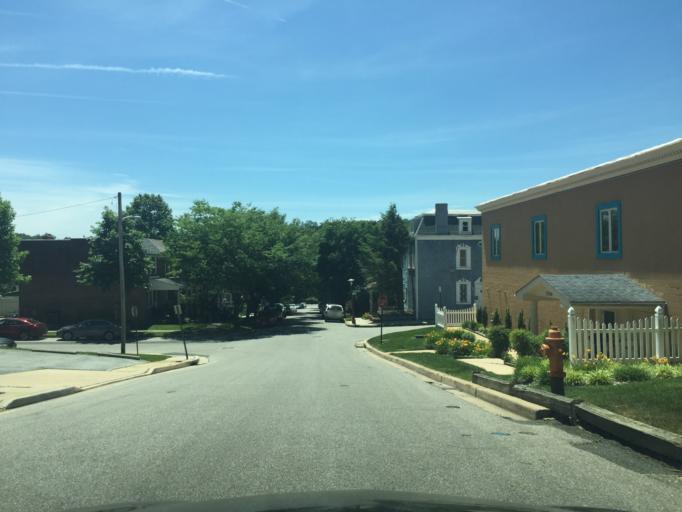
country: US
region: Maryland
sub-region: City of Baltimore
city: Baltimore
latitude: 39.3334
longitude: -76.6514
